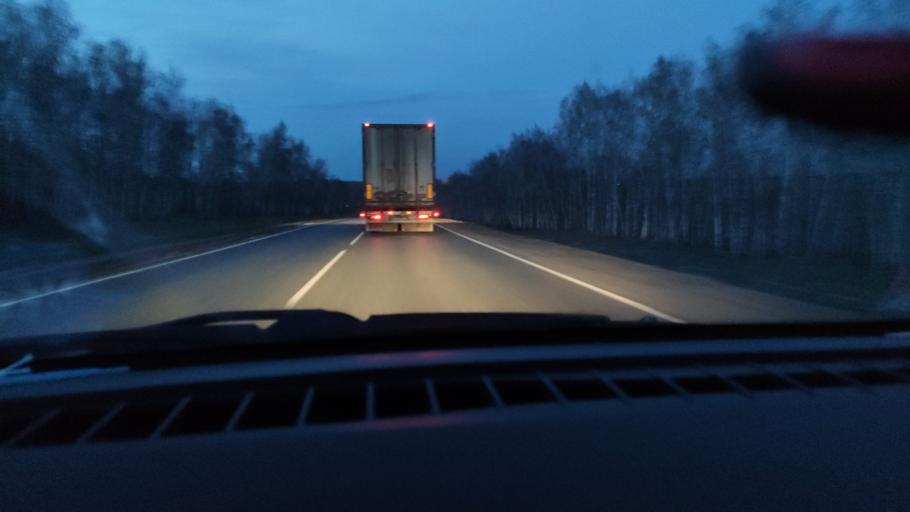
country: RU
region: Saratov
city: Sennoy
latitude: 52.1232
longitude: 46.8495
